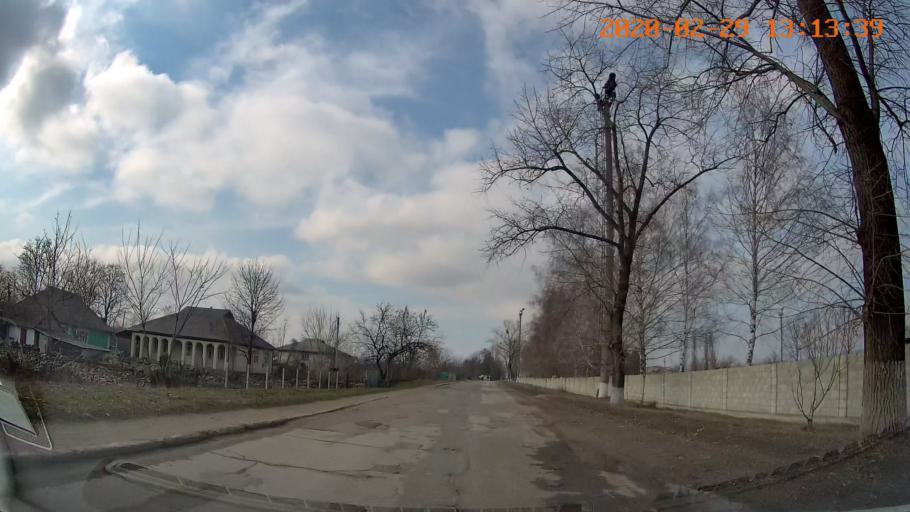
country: MD
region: Telenesti
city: Camenca
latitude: 48.0147
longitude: 28.6814
